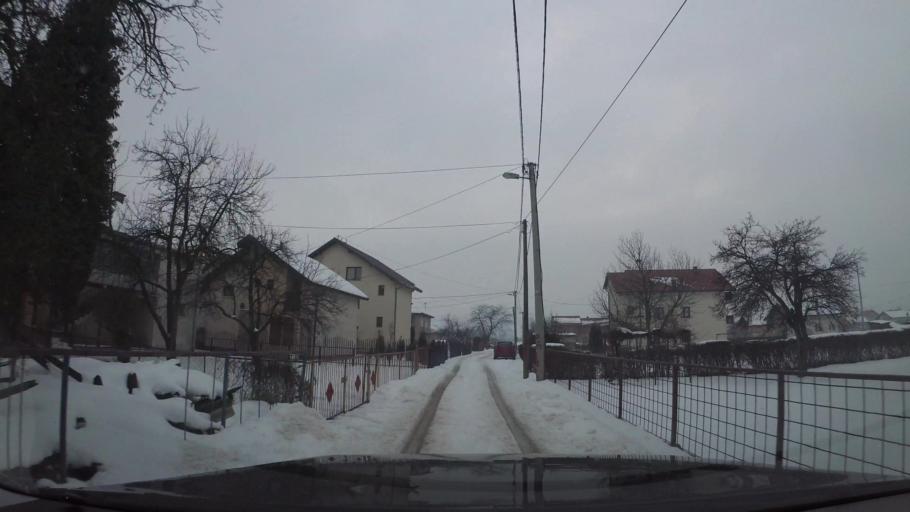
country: BA
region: Federation of Bosnia and Herzegovina
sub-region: Kanton Sarajevo
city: Sarajevo
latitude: 43.8507
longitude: 18.3009
